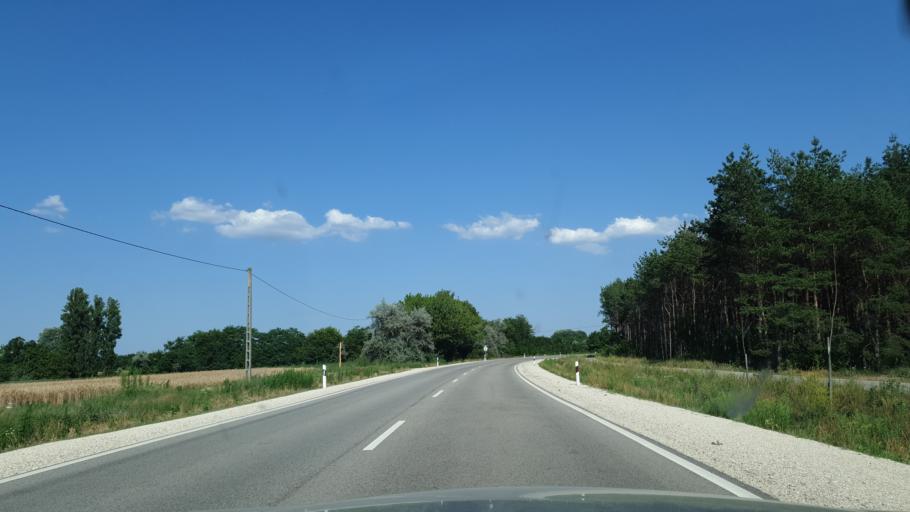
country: HU
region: Csongrad
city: Asotthalom
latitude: 46.2297
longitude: 19.7513
